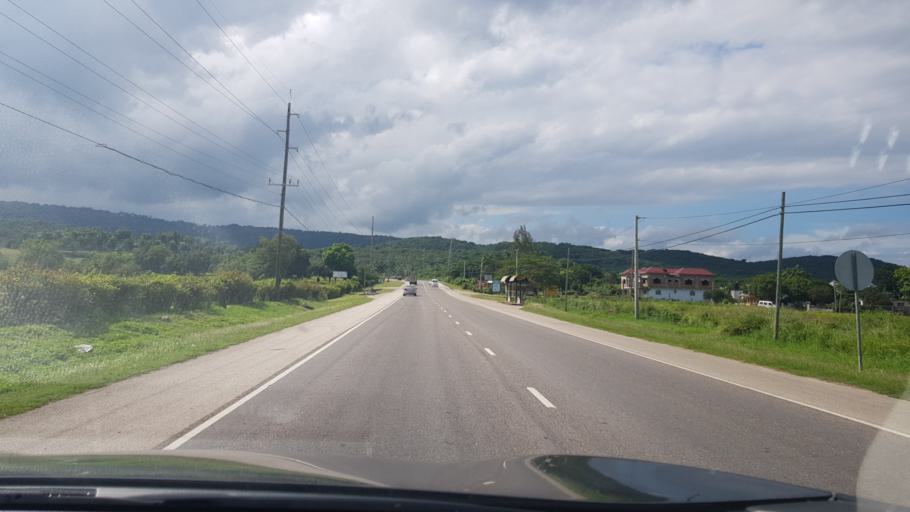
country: JM
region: Trelawny
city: Duncans
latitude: 18.4726
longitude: -77.4917
